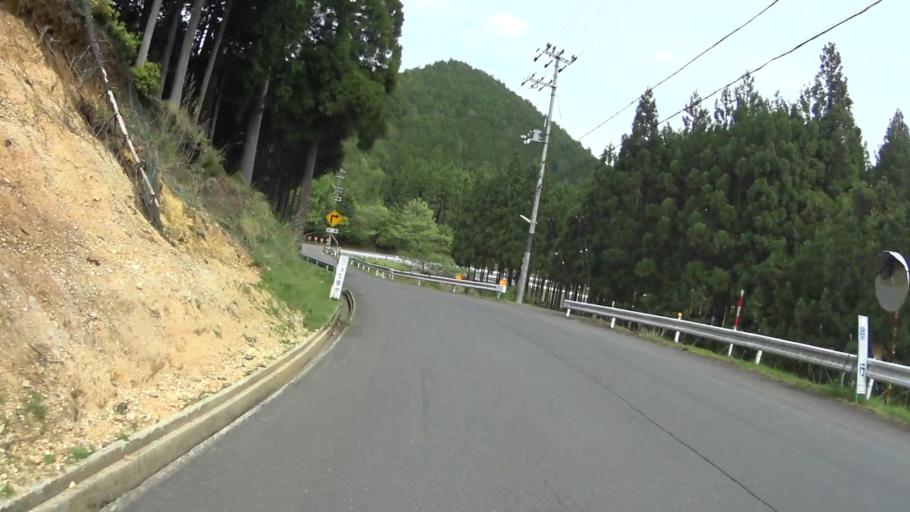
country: JP
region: Kyoto
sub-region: Kyoto-shi
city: Kamigyo-ku
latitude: 35.1865
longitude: 135.6515
